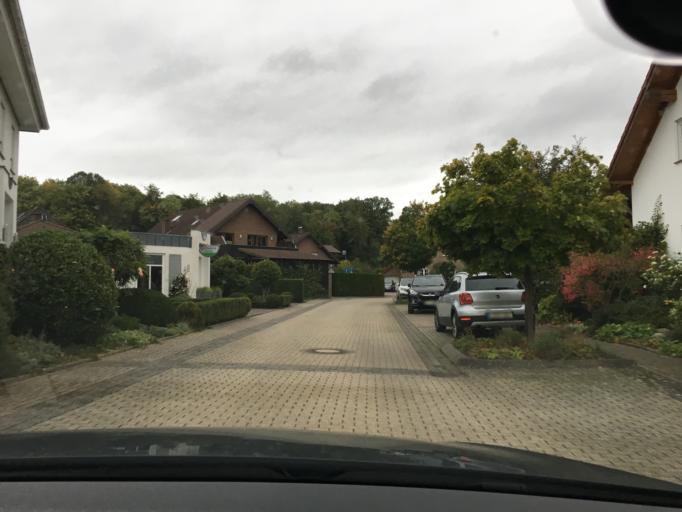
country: DE
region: North Rhine-Westphalia
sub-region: Regierungsbezirk Koln
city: Kreuzau
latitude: 50.7411
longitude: 6.4972
